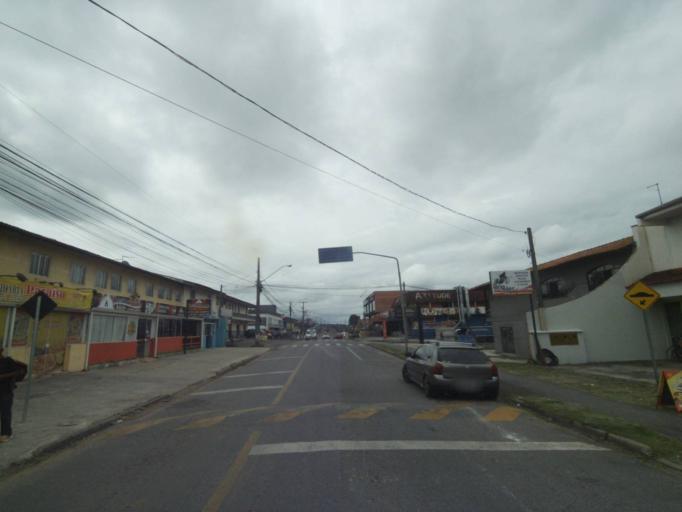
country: BR
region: Parana
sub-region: Quatro Barras
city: Quatro Barras
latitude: -25.3578
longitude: -49.1099
